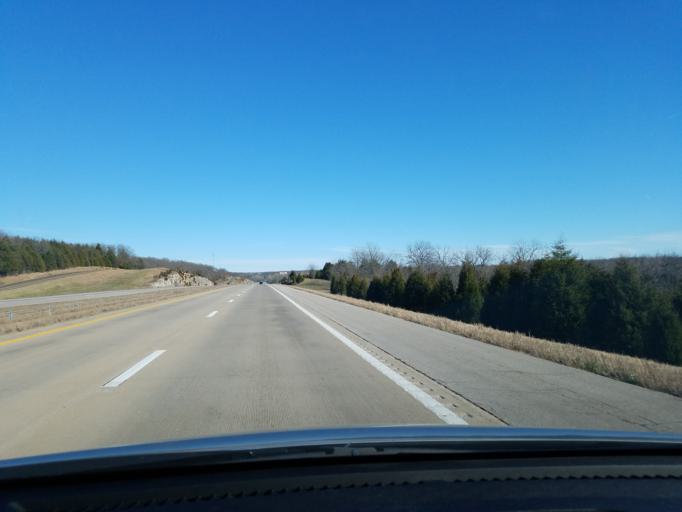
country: US
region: Missouri
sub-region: Laclede County
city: Lebanon
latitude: 37.7579
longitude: -92.5408
